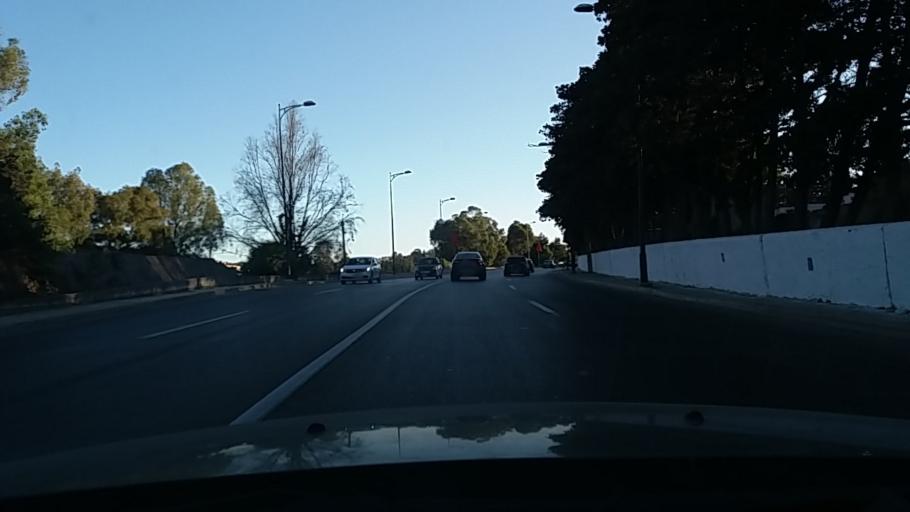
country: MA
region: Tanger-Tetouan
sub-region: Tanger-Assilah
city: Tangier
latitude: 35.7804
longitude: -5.8431
